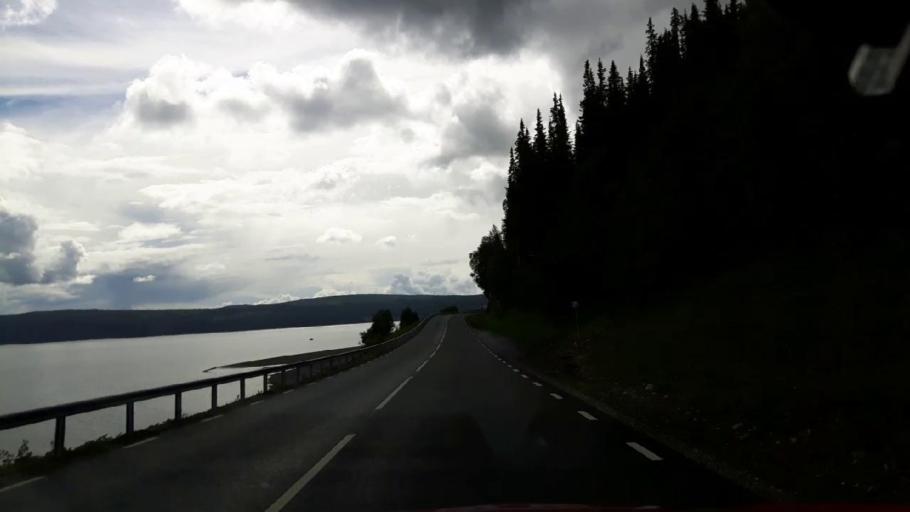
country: NO
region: Nord-Trondelag
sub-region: Royrvik
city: Royrvik
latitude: 64.8272
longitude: 14.0789
